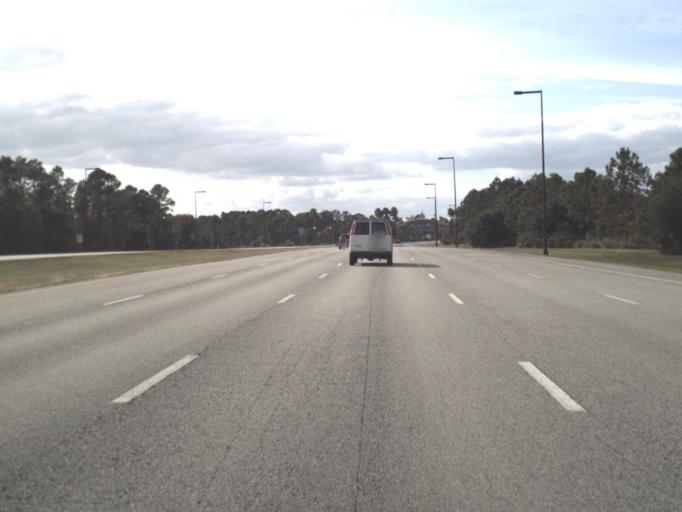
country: US
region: Florida
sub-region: Osceola County
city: Celebration
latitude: 28.3458
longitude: -81.5397
